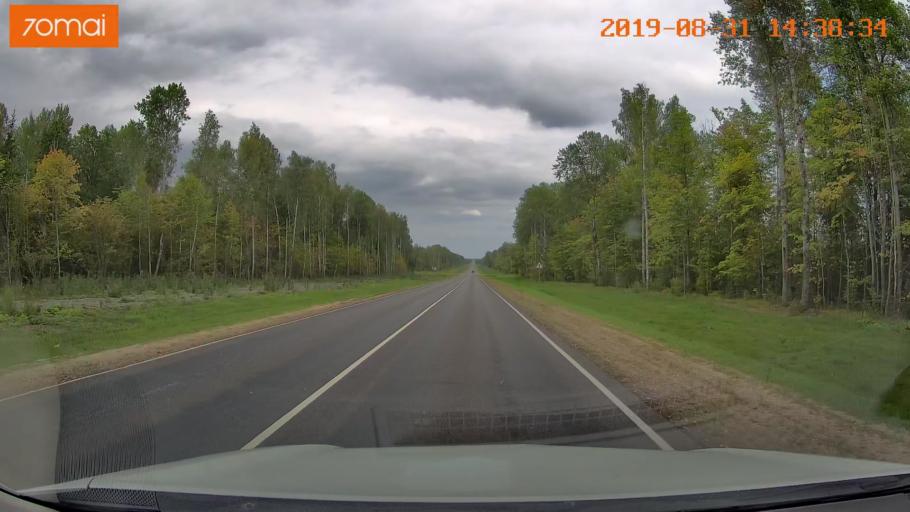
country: RU
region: Smolensk
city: Yekimovichi
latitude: 54.1853
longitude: 33.5312
